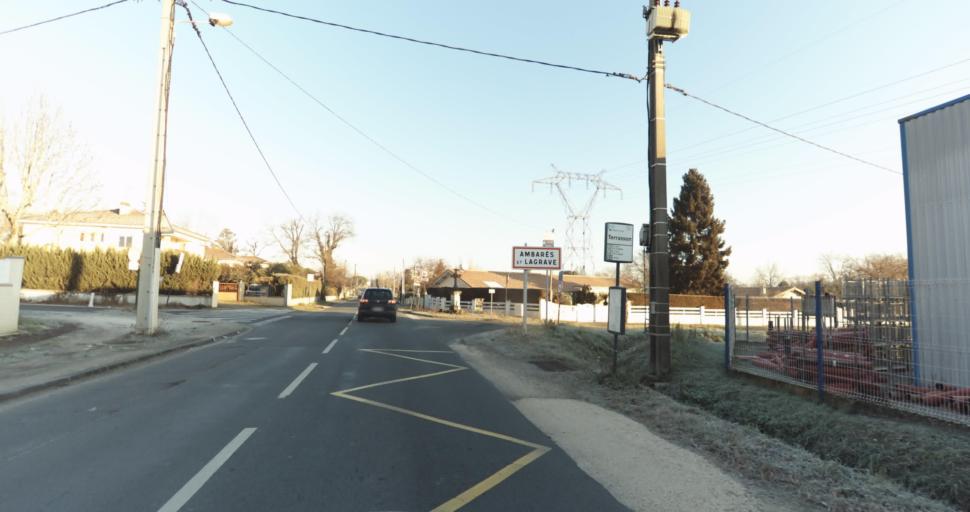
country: FR
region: Aquitaine
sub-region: Departement de la Gironde
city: Ambares-et-Lagrave
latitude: 44.9163
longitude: -0.4930
